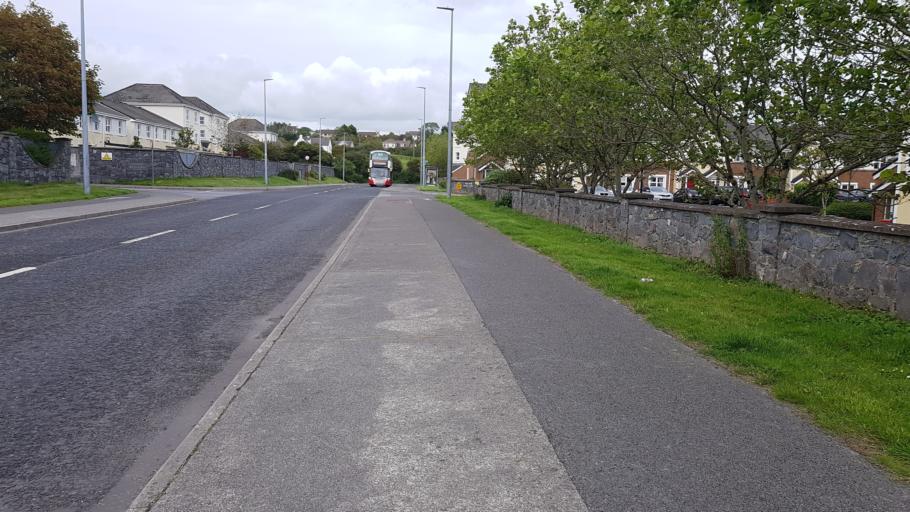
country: IE
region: Connaught
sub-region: County Galway
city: Gaillimh
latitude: 53.2982
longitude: -9.0253
